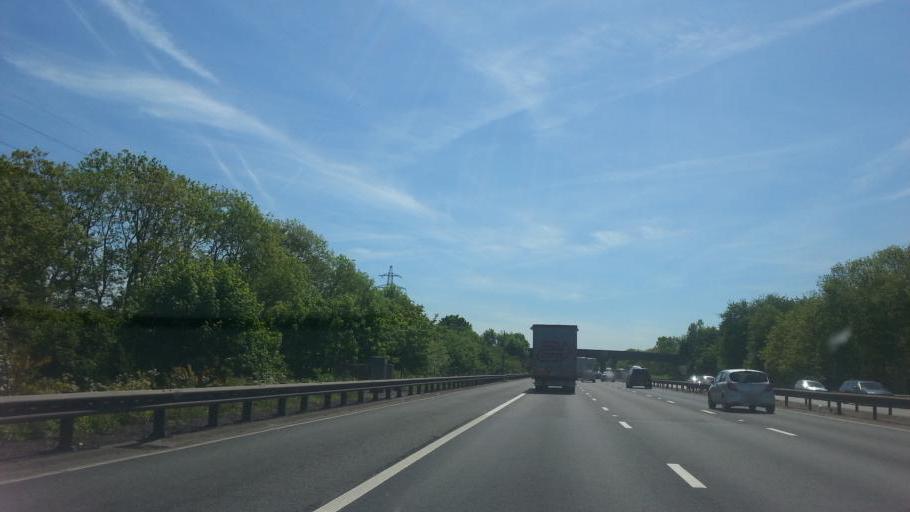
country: GB
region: England
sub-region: Central Bedfordshire
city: Steppingley
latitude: 51.9958
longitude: -0.5388
